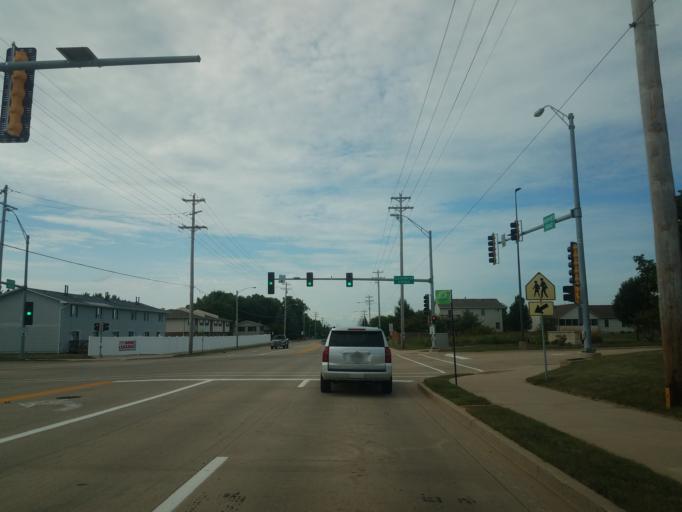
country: US
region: Illinois
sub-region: McLean County
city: Normal
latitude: 40.4955
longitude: -88.9239
